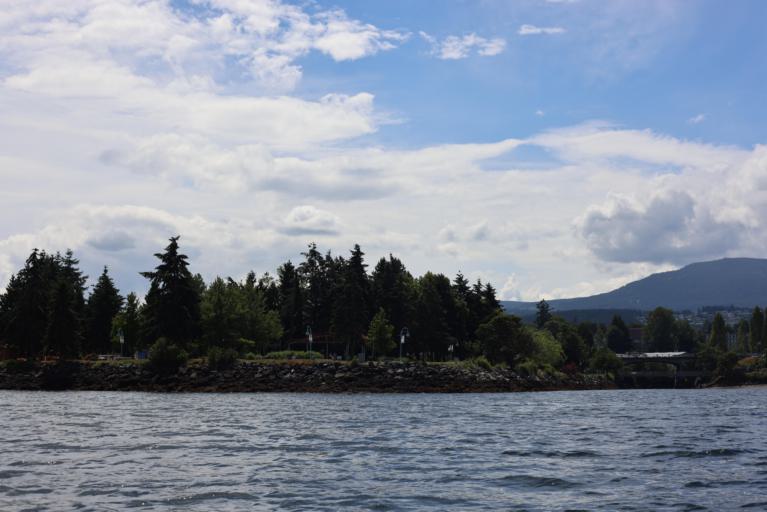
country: CA
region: British Columbia
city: Nanaimo
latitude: 49.1742
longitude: -123.9367
